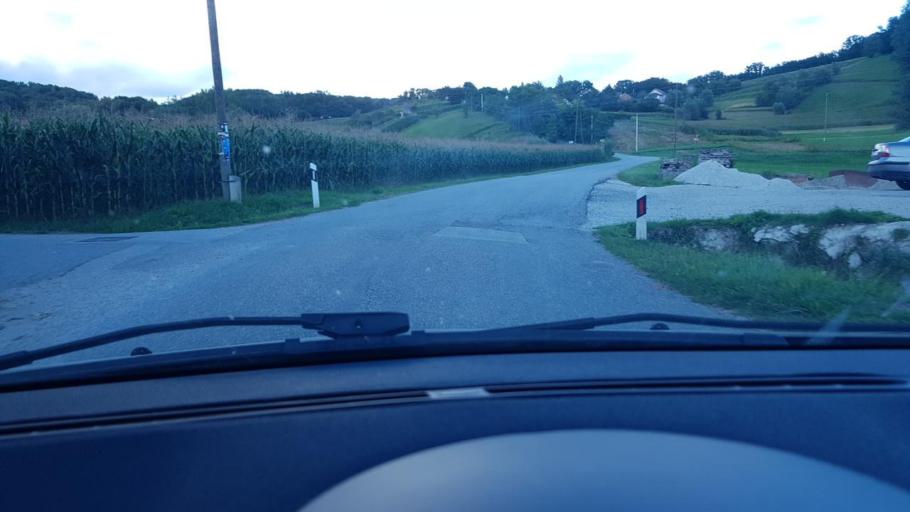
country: HR
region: Krapinsko-Zagorska
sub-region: Grad Krapina
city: Krapina
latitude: 46.1559
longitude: 15.8264
